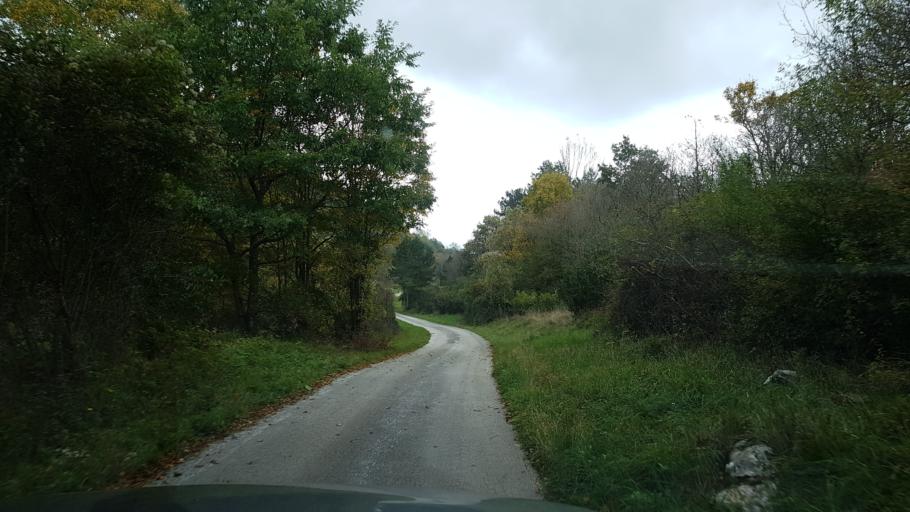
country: HR
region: Istarska
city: Buzet
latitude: 45.4395
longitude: 14.0510
